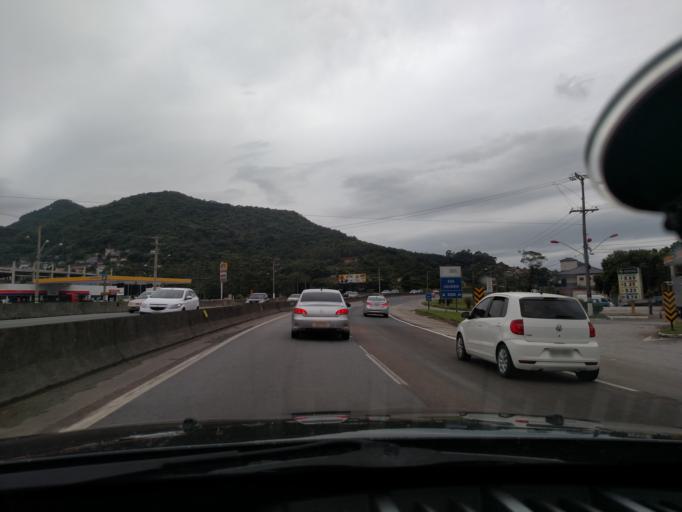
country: BR
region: Santa Catarina
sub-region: Biguacu
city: Biguacu
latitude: -27.4902
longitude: -48.6562
